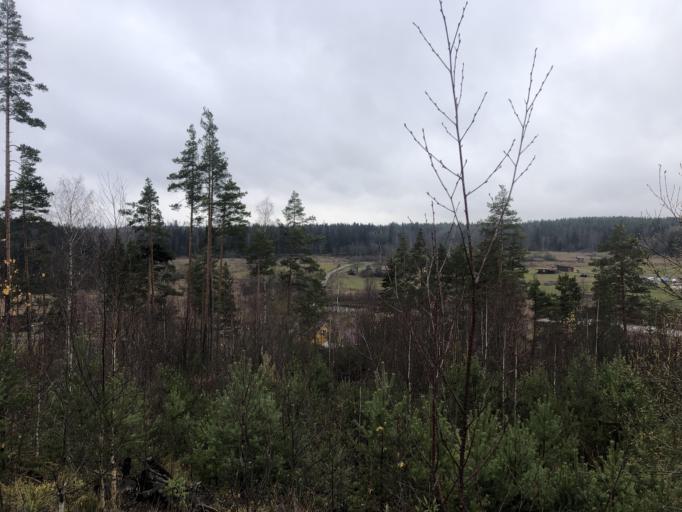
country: RU
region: Leningrad
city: Kuznechnoye
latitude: 61.2158
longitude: 29.9234
